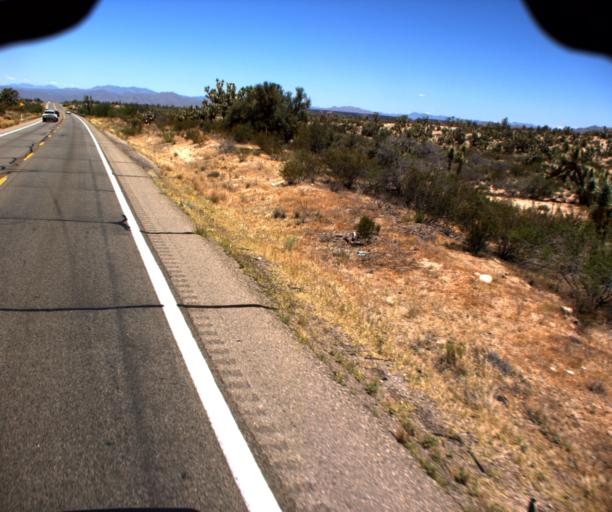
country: US
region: Arizona
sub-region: Yavapai County
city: Congress
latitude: 34.2700
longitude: -113.0940
